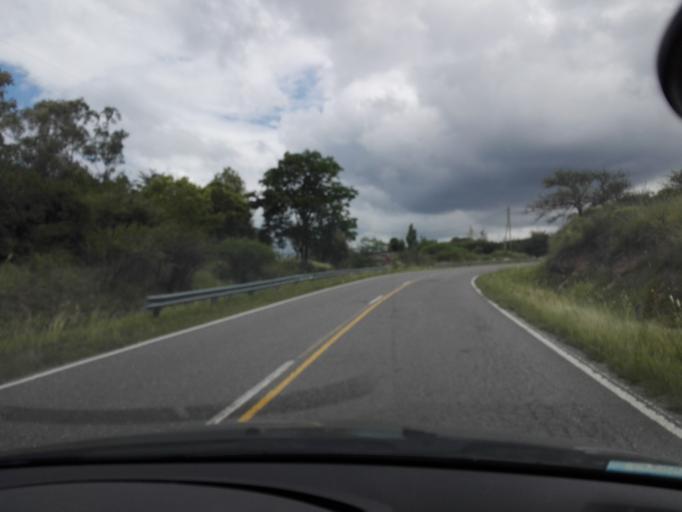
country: AR
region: Cordoba
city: Alta Gracia
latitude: -31.5921
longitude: -64.4828
